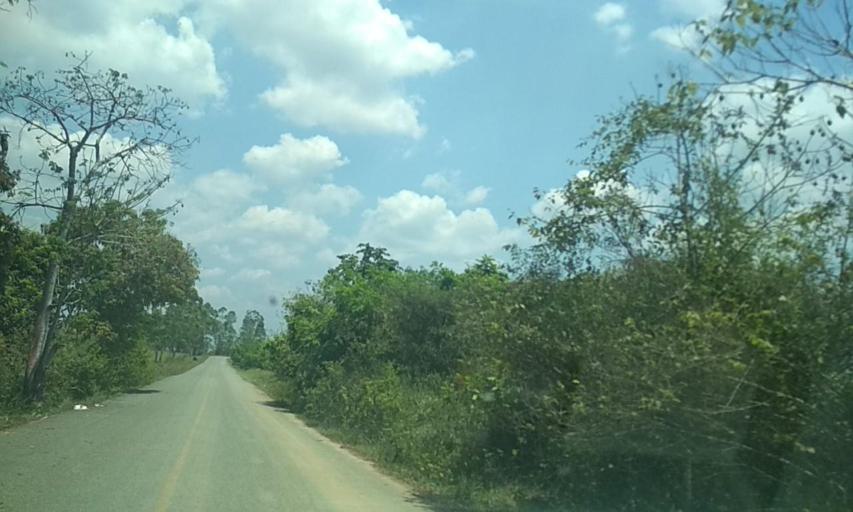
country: MX
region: Tabasco
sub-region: Huimanguillo
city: Francisco Rueda
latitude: 17.8068
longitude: -93.8651
